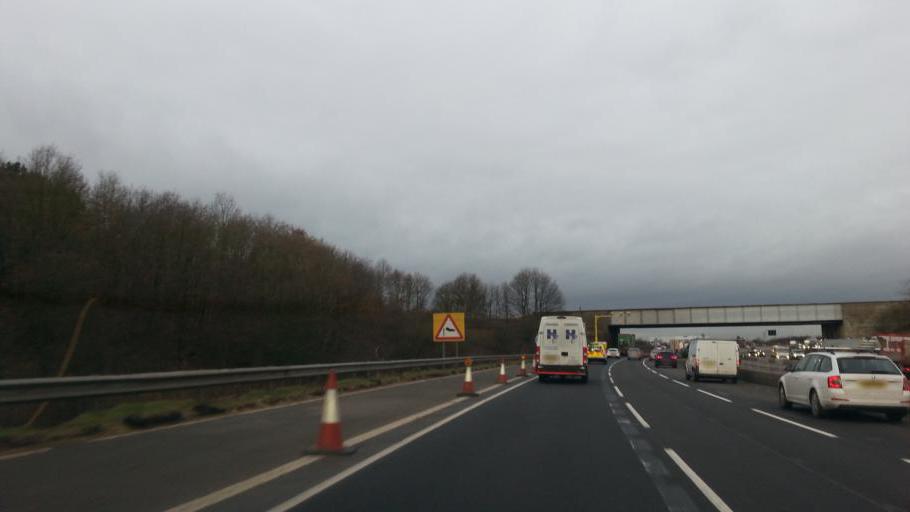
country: GB
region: England
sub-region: City and Borough of Wakefield
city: Normanton
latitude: 53.7101
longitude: -1.4117
